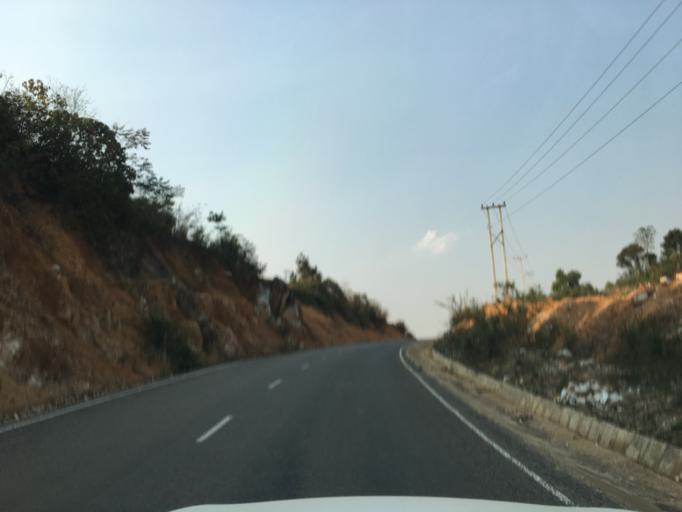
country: LA
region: Houaphan
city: Xam Nua
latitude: 20.5740
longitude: 104.0565
